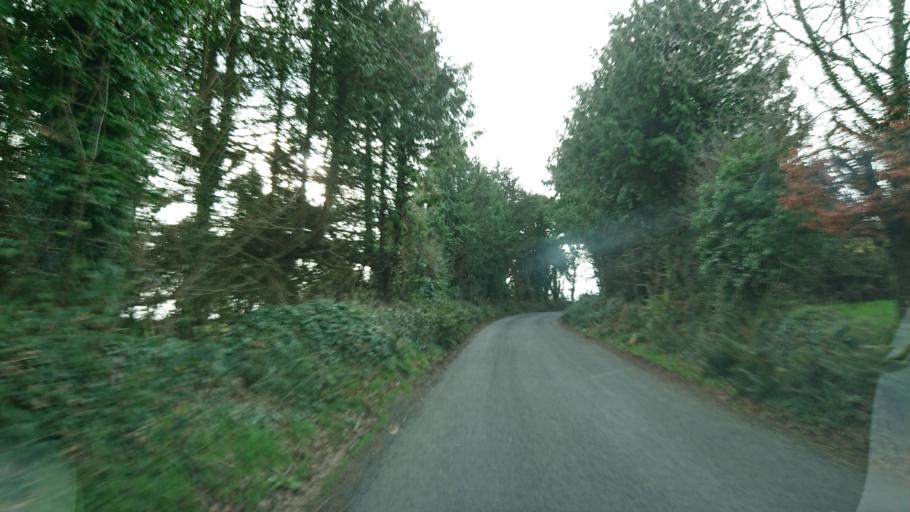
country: IE
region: Munster
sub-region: Waterford
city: Tra Mhor
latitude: 52.1761
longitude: -7.1746
